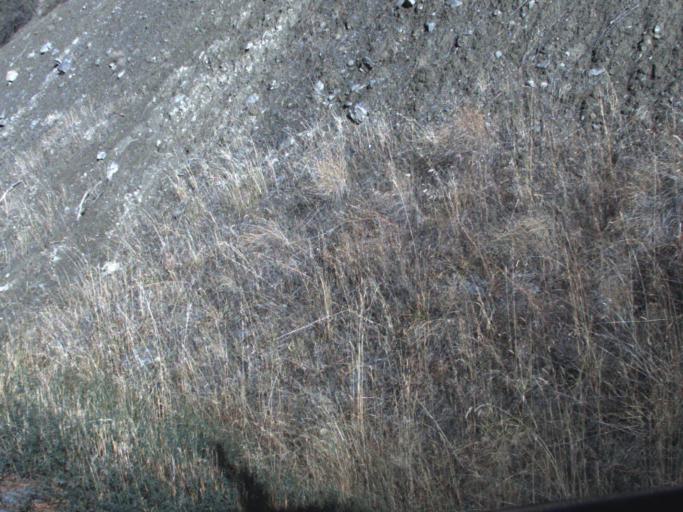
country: US
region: Washington
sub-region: Stevens County
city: Kettle Falls
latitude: 48.1860
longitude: -118.1710
